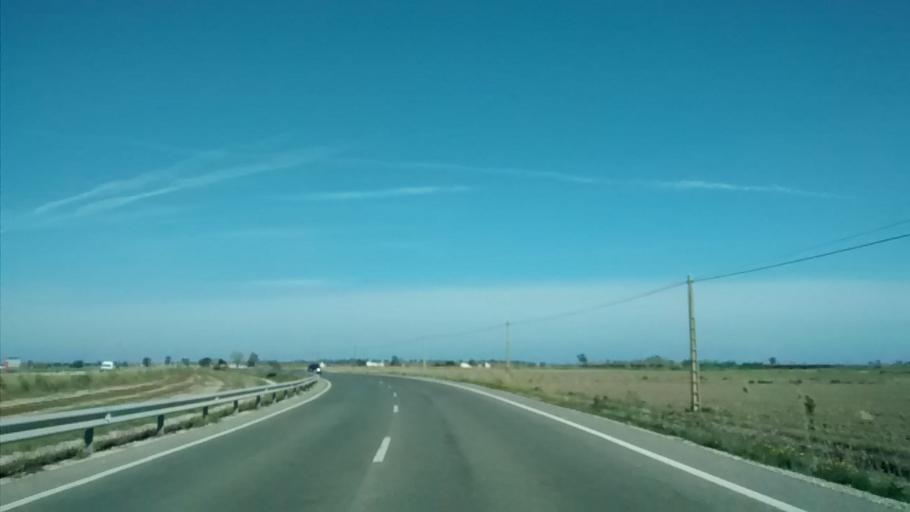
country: ES
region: Catalonia
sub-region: Provincia de Tarragona
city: Deltebre
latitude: 40.7044
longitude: 0.7914
